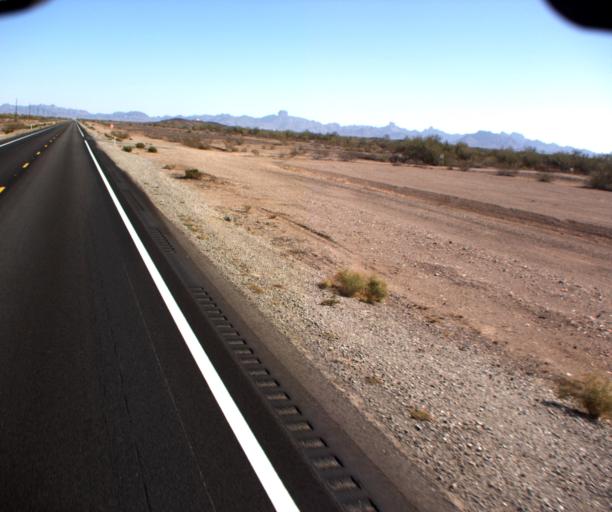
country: US
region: Arizona
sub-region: Yuma County
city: Fortuna Foothills
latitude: 32.9494
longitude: -114.3001
